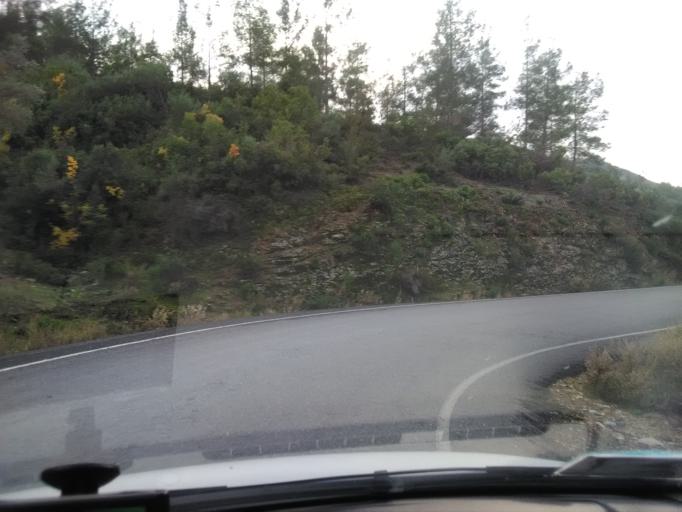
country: TR
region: Antalya
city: Gazipasa
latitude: 36.2912
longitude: 32.3776
